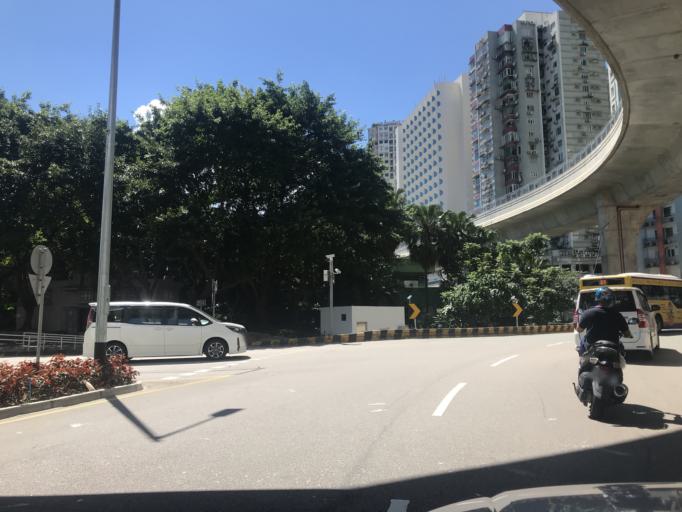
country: MO
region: Macau
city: Macau
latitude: 22.1560
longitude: 113.5531
